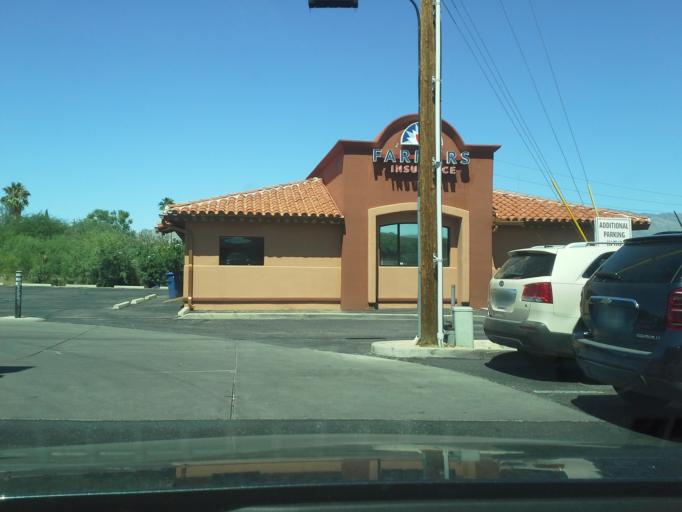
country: US
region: Arizona
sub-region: Pima County
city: Tucson
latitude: 32.2365
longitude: -110.9271
